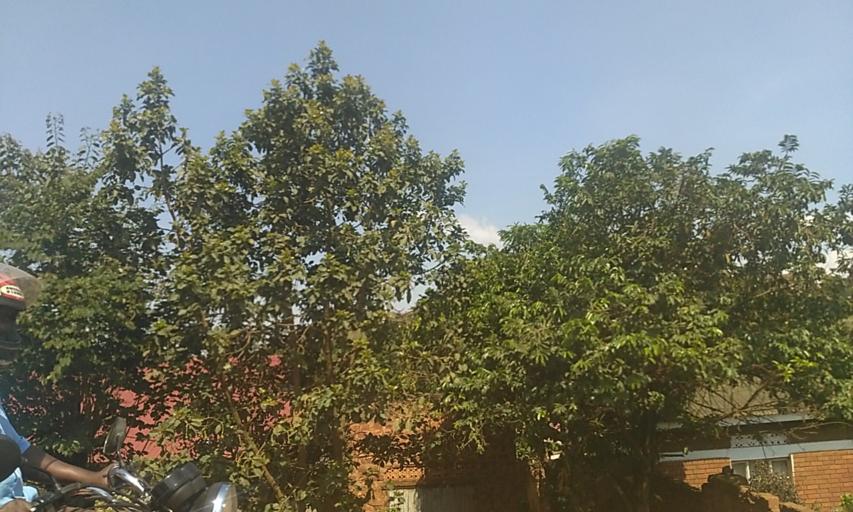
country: UG
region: Central Region
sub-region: Wakiso District
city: Kireka
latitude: 0.3702
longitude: 32.6024
